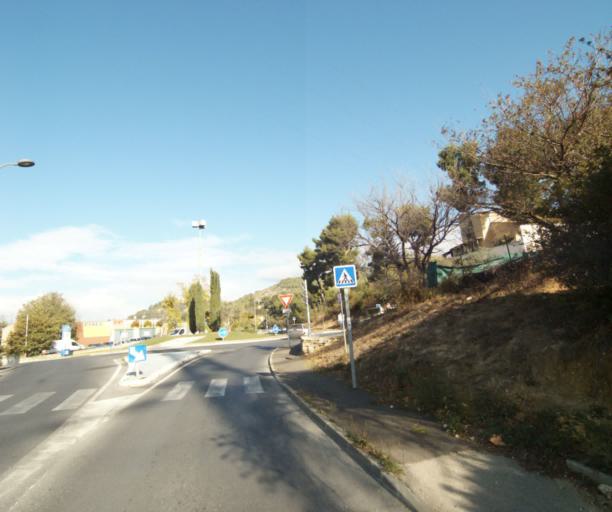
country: FR
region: Provence-Alpes-Cote d'Azur
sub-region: Departement des Bouches-du-Rhone
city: Allauch
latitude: 43.3274
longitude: 5.4906
